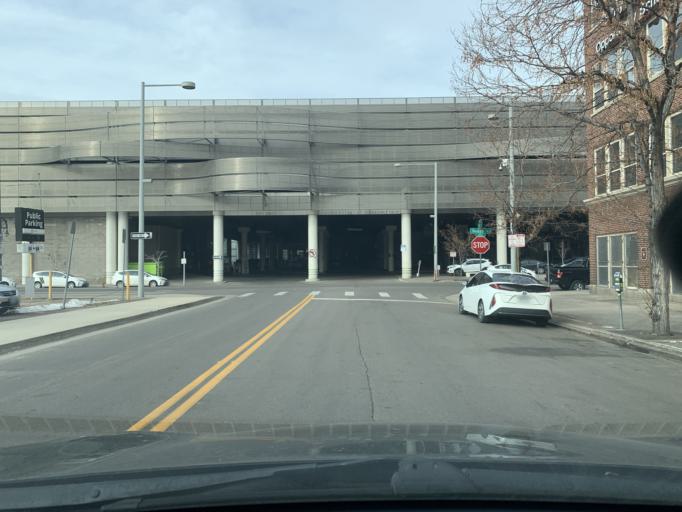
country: US
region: Colorado
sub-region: Denver County
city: Denver
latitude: 39.7406
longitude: -104.9958
